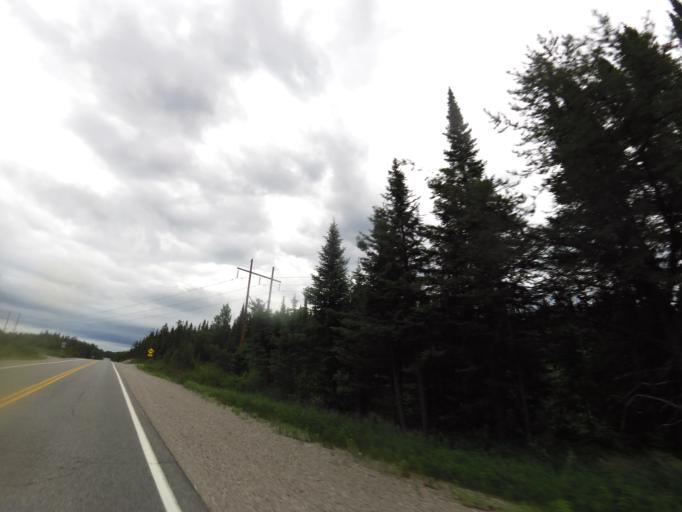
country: CA
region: Quebec
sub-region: Abitibi-Temiscamingue
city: Amos
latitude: 48.9586
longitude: -77.9554
